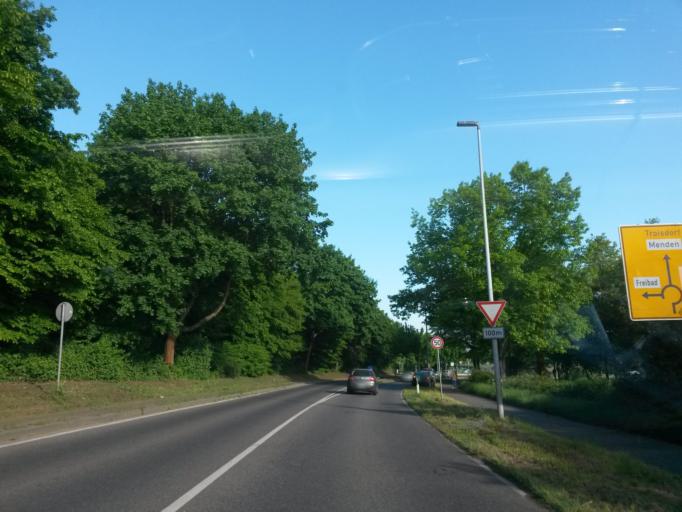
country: DE
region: North Rhine-Westphalia
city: Sankt Augustin
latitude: 50.7765
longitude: 7.1751
